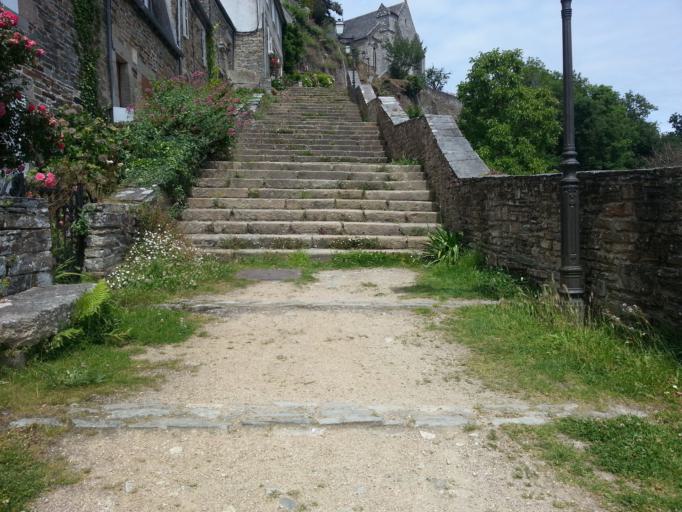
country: FR
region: Brittany
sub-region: Departement des Cotes-d'Armor
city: Lannion
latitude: 48.7352
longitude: -3.4592
